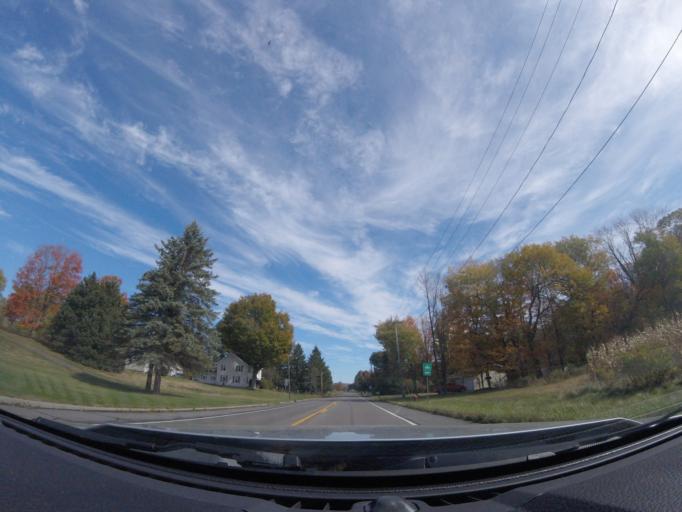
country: US
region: New York
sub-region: Cortland County
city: Cortland West
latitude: 42.5753
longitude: -76.2429
